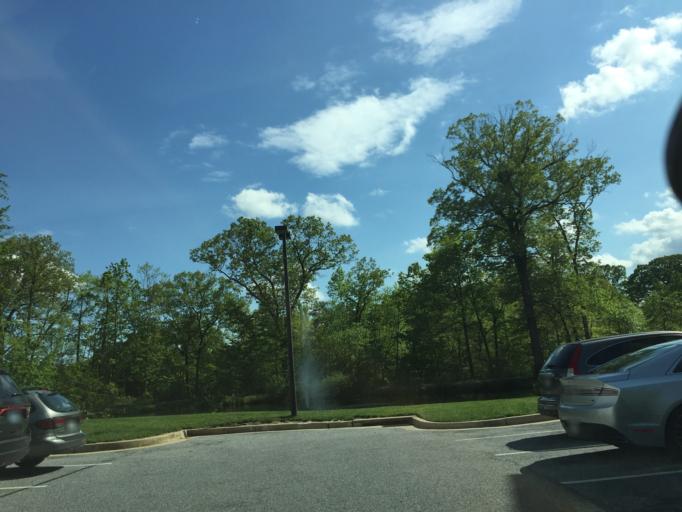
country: US
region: Maryland
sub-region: Baltimore County
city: Middle River
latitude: 39.3173
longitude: -76.4433
